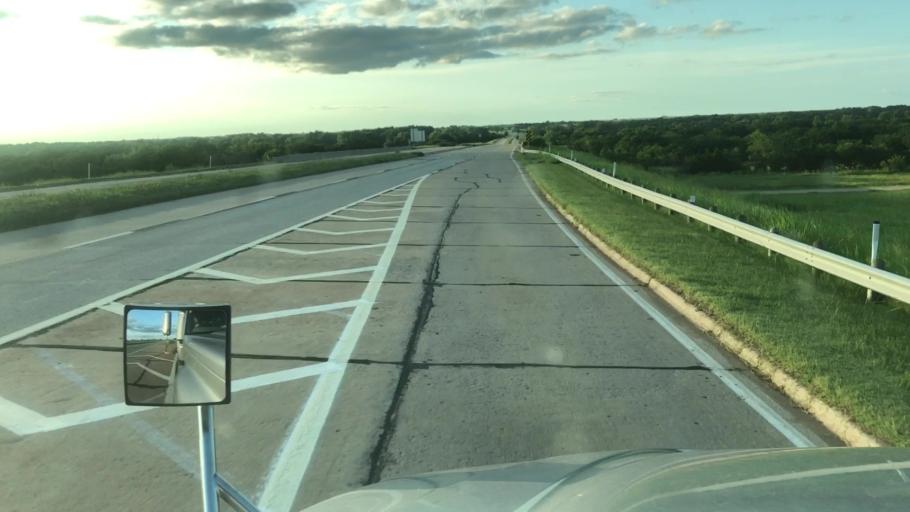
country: US
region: Oklahoma
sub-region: Pawnee County
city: Pawnee
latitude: 36.2965
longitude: -96.9862
